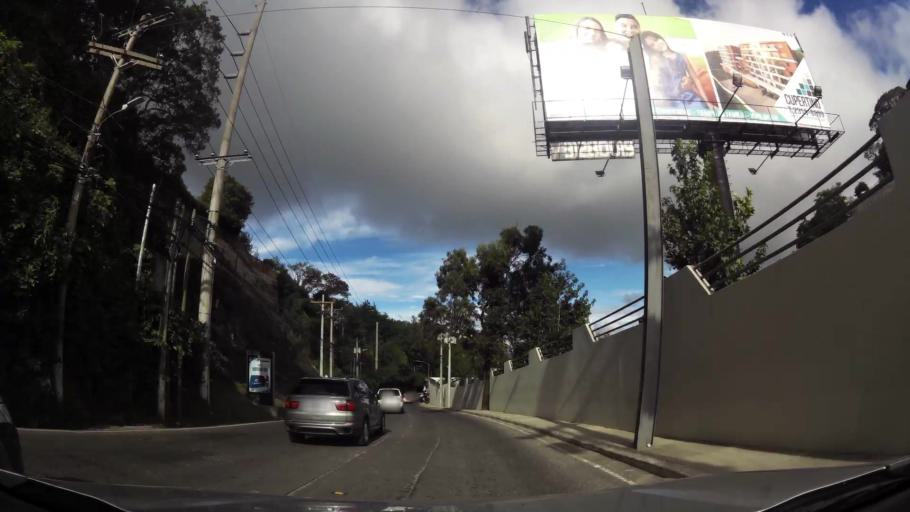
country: GT
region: Guatemala
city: Santa Catarina Pinula
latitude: 14.5712
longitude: -90.4871
